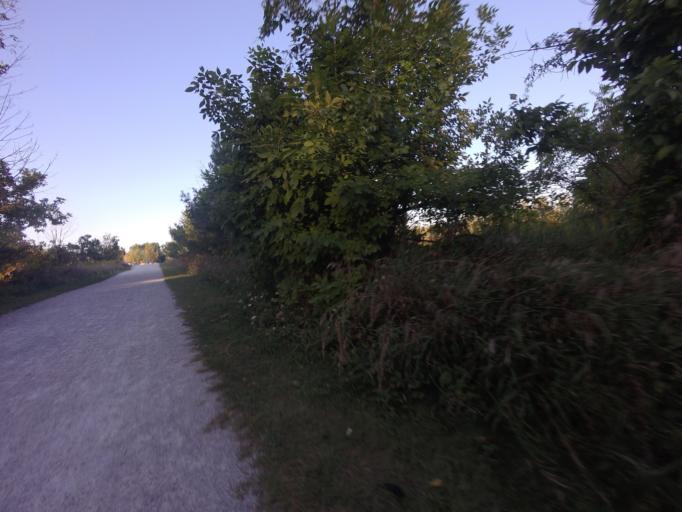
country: CA
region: Ontario
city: Brampton
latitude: 43.8732
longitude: -79.8593
